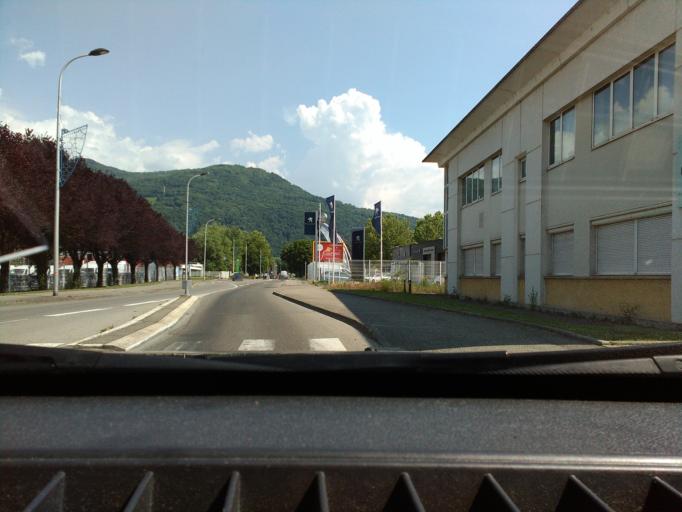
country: FR
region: Rhone-Alpes
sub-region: Departement de l'Isere
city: Saint-Martin-d'Heres
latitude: 45.1706
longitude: 5.7524
